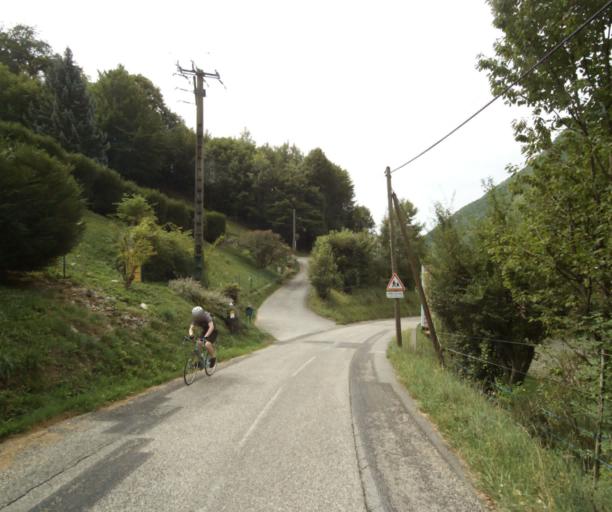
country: FR
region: Rhone-Alpes
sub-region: Departement de l'Isere
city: Saint-Egreve
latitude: 45.2785
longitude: 5.7084
